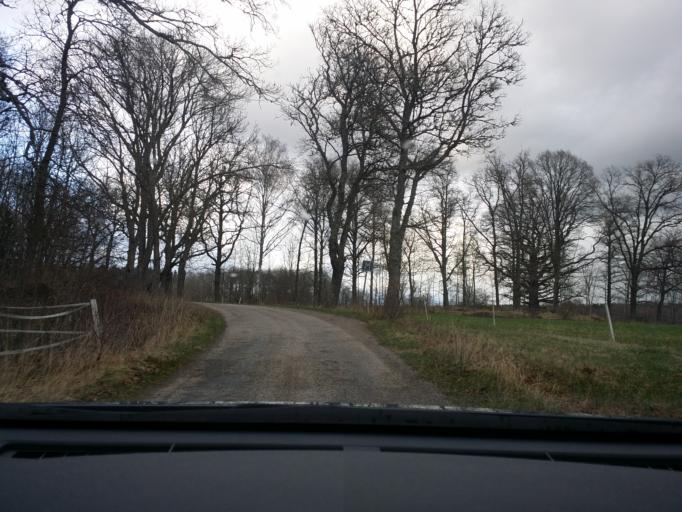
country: SE
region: Soedermanland
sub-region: Eskilstuna Kommun
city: Arla
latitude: 59.3843
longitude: 16.6491
